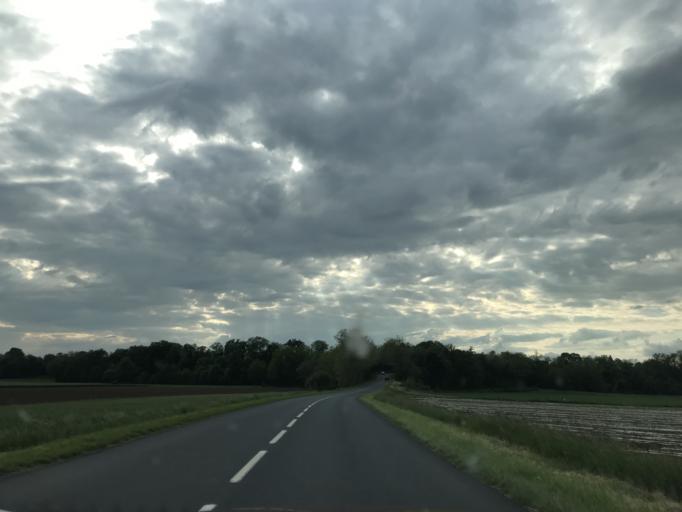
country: FR
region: Auvergne
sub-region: Departement du Puy-de-Dome
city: Maringues
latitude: 45.9176
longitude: 3.3505
